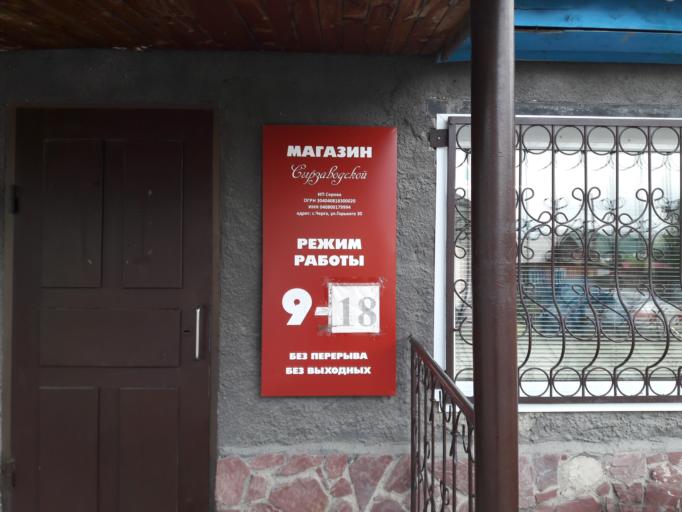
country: RU
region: Altay
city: Cherga
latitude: 51.5700
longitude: 85.5622
